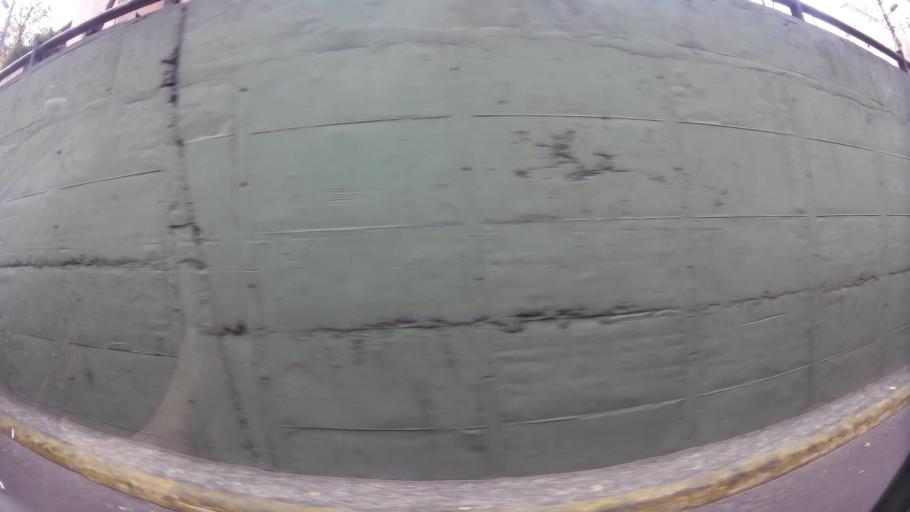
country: EC
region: Pichincha
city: Quito
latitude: -0.2204
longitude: -78.5195
